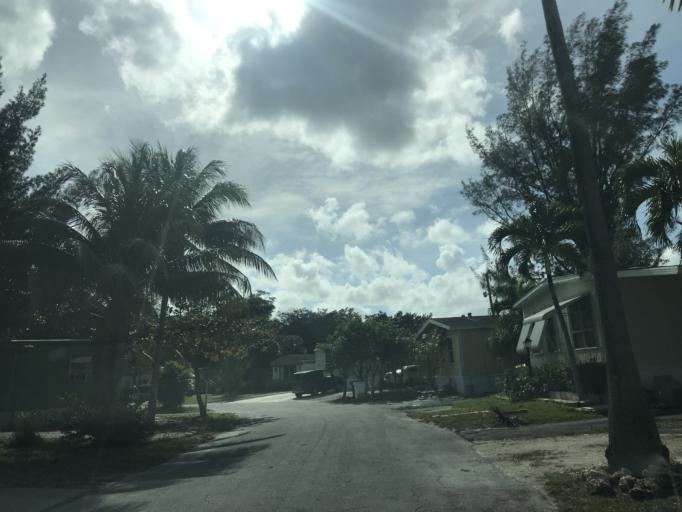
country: US
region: Florida
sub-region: Palm Beach County
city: Boca Pointe
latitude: 26.3099
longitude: -80.1766
